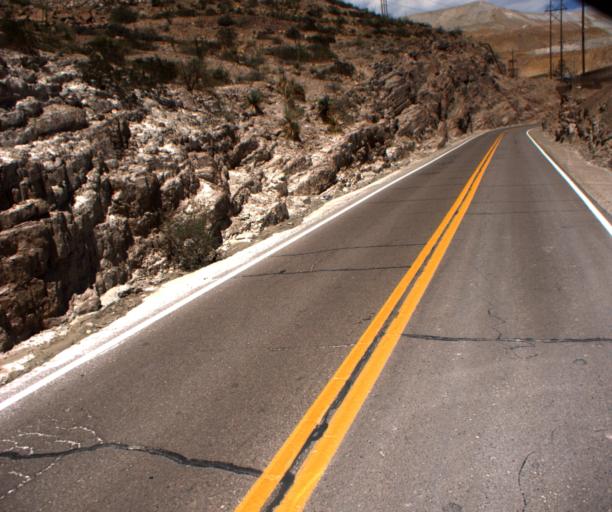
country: US
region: Arizona
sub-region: Greenlee County
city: Morenci
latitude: 33.0692
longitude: -109.3447
